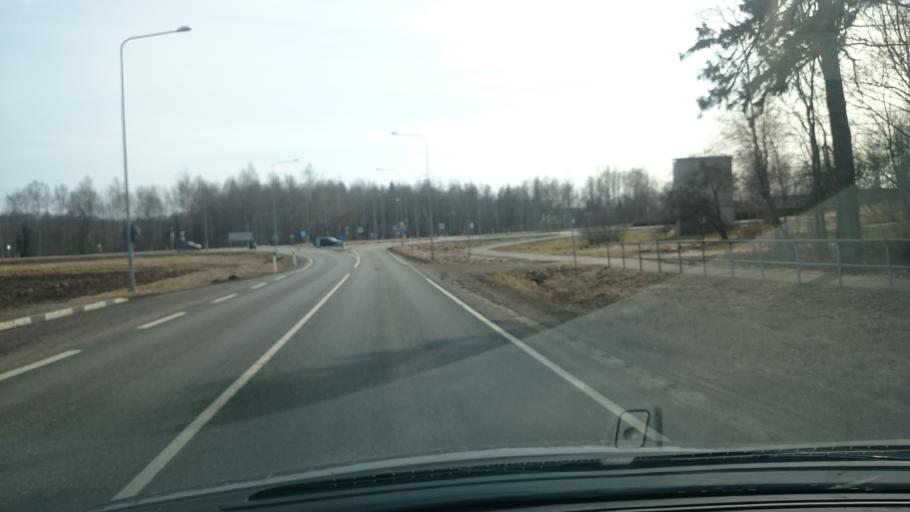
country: EE
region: Jaervamaa
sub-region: Paide linn
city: Paide
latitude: 58.8811
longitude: 25.5179
